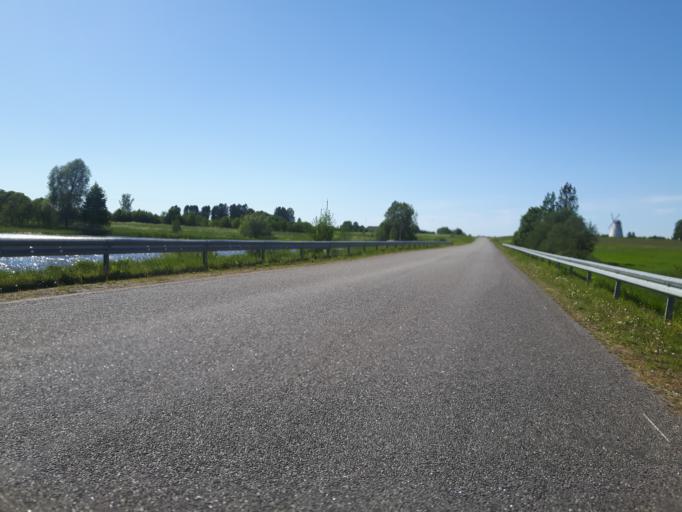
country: EE
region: Laeaene-Virumaa
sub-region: Haljala vald
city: Haljala
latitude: 59.5431
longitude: 26.1835
